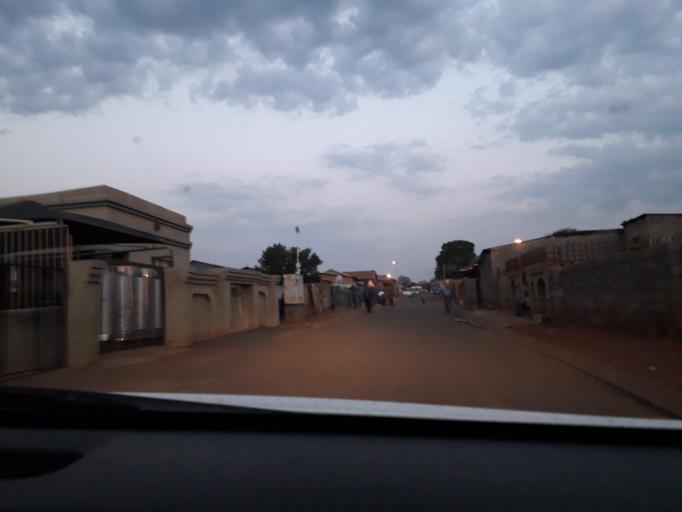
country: ZA
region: Gauteng
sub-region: Ekurhuleni Metropolitan Municipality
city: Tembisa
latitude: -25.9992
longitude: 28.2389
